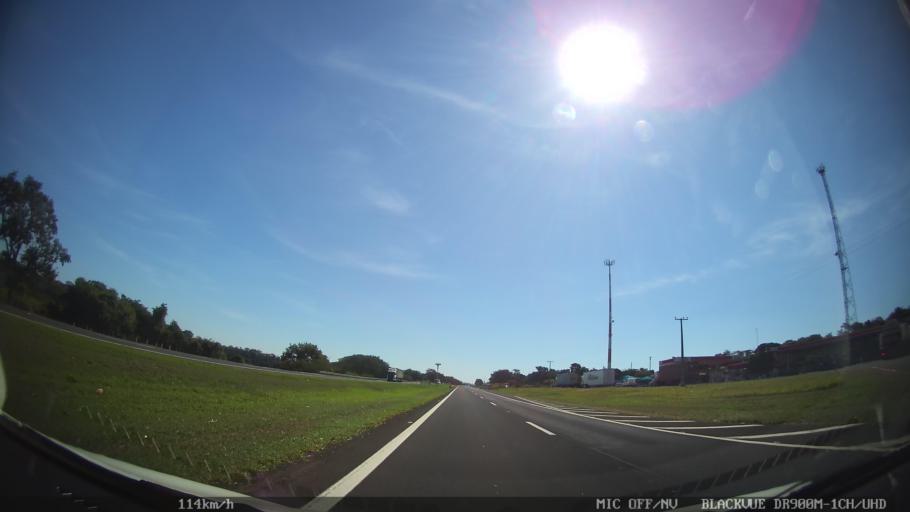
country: BR
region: Sao Paulo
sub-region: Sao Simao
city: Sao Simao
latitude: -21.5552
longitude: -47.6367
